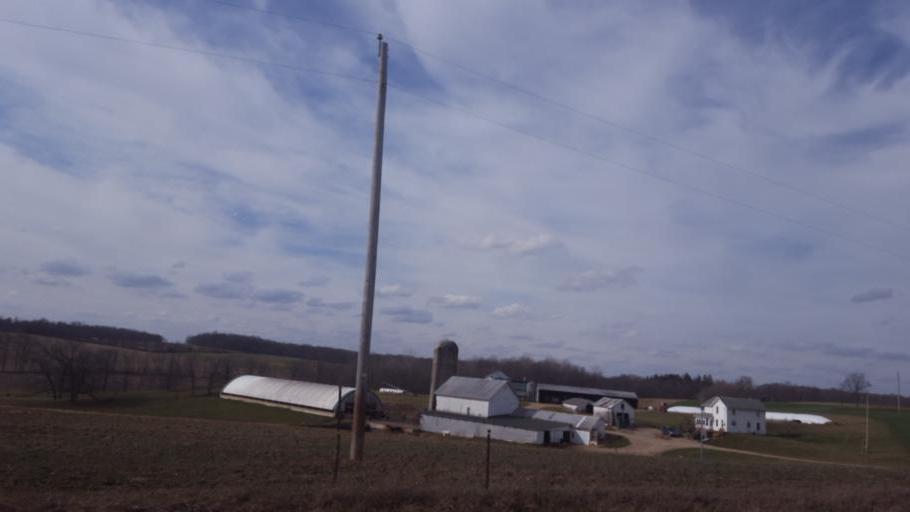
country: US
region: Ohio
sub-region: Knox County
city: Fredericktown
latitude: 40.5053
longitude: -82.4243
